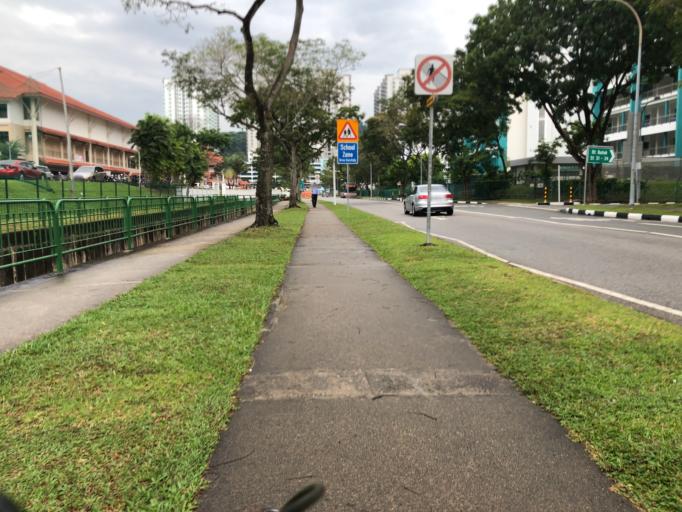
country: MY
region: Johor
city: Johor Bahru
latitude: 1.3653
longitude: 103.7483
